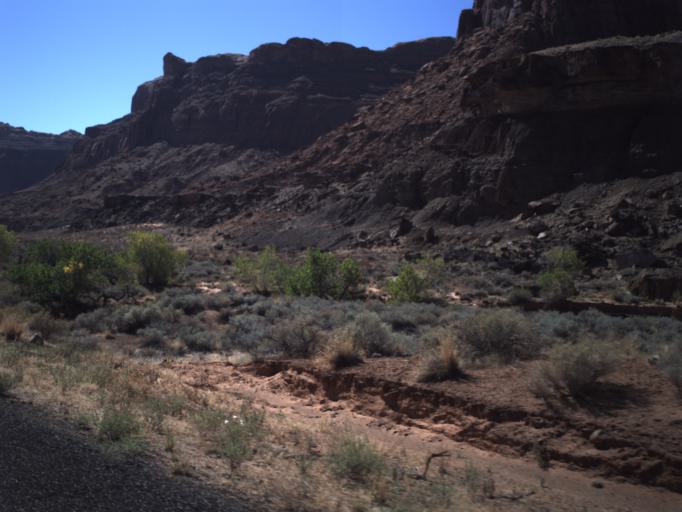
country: US
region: Utah
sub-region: San Juan County
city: Blanding
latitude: 37.9178
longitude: -110.4625
